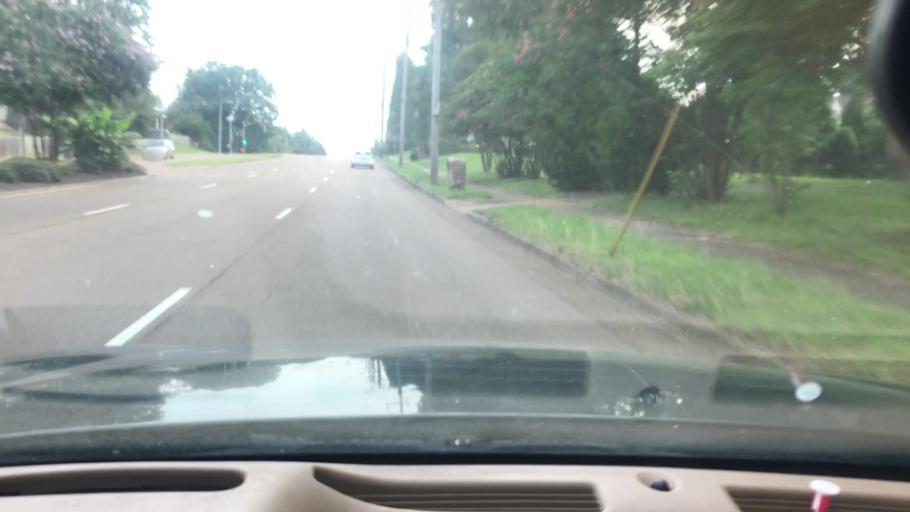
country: US
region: Tennessee
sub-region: Shelby County
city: Bartlett
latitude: 35.1889
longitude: -89.8692
